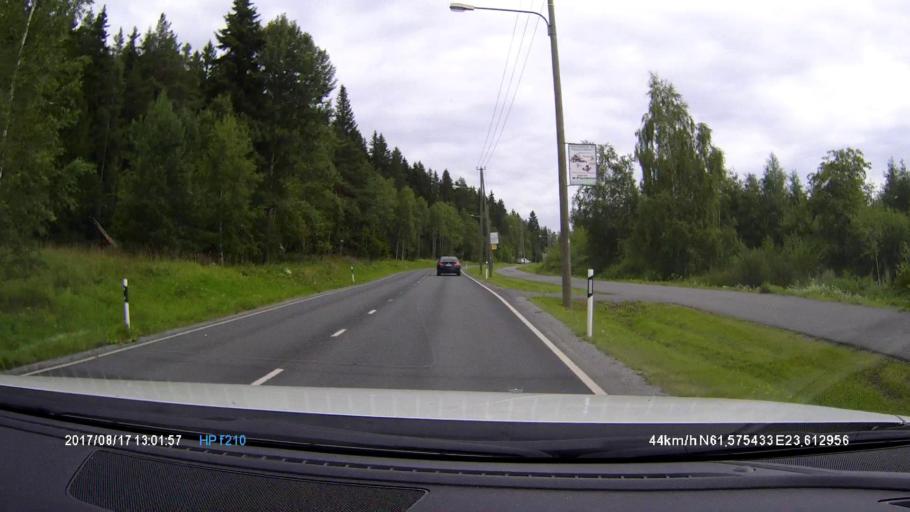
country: FI
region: Pirkanmaa
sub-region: Tampere
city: Yloejaervi
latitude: 61.5756
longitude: 23.6146
